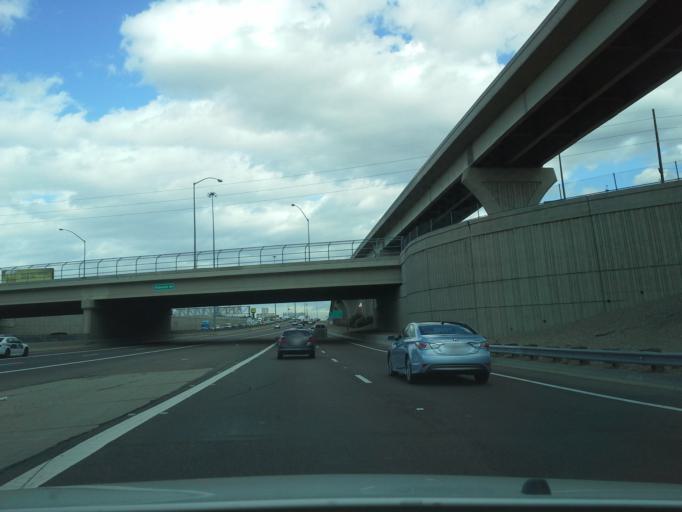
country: US
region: Arizona
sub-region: Maricopa County
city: Phoenix
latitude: 33.4651
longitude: -112.1094
